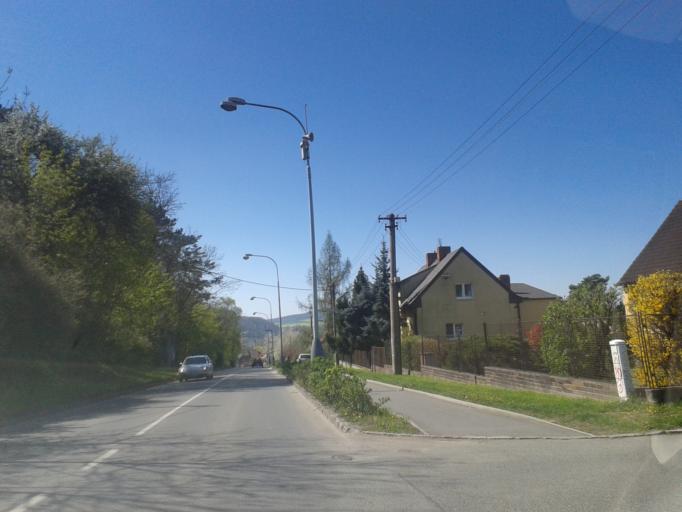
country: CZ
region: Central Bohemia
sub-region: Okres Beroun
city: Beroun
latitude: 49.9635
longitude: 14.0621
